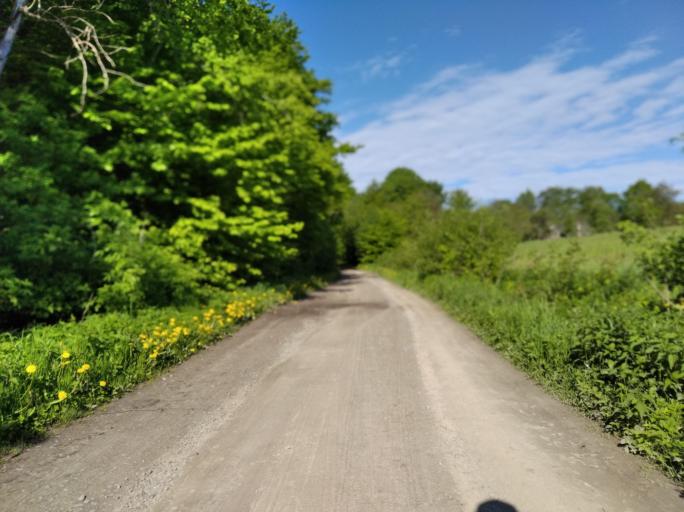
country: PL
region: Subcarpathian Voivodeship
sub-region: Powiat strzyzowski
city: Frysztak
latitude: 49.8400
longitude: 21.5631
